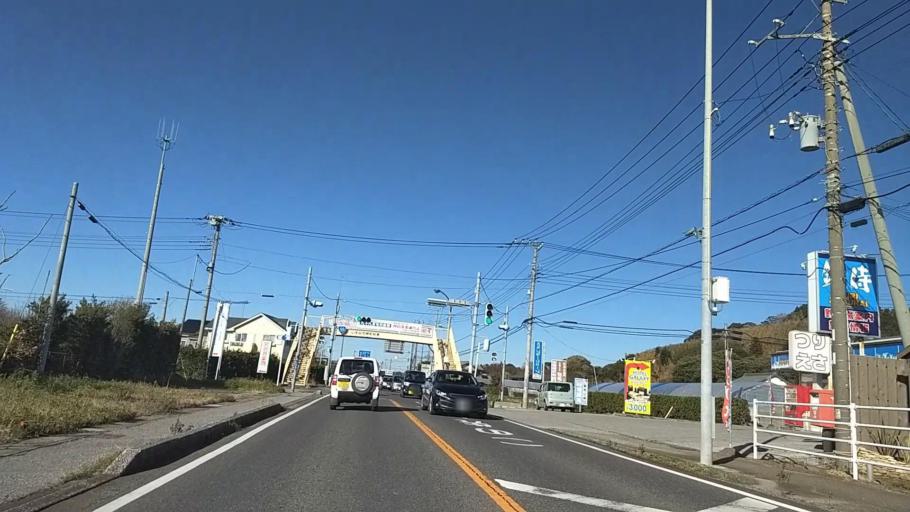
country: JP
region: Chiba
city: Ohara
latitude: 35.3115
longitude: 140.4027
